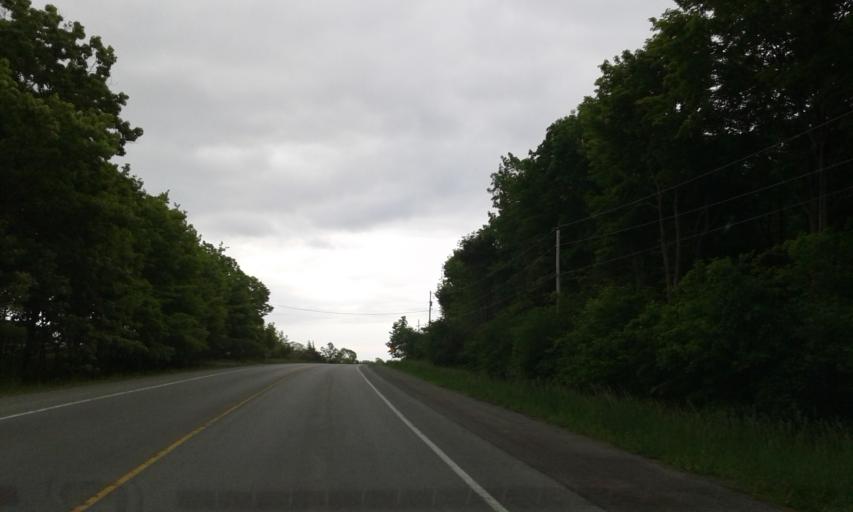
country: CA
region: Ontario
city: Quinte West
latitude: 43.9737
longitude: -77.5046
